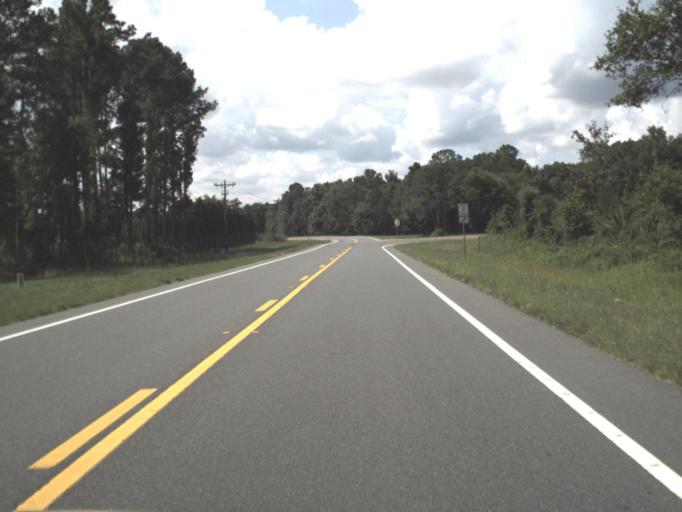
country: US
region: Florida
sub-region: Alachua County
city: Alachua
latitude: 29.8431
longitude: -82.3472
